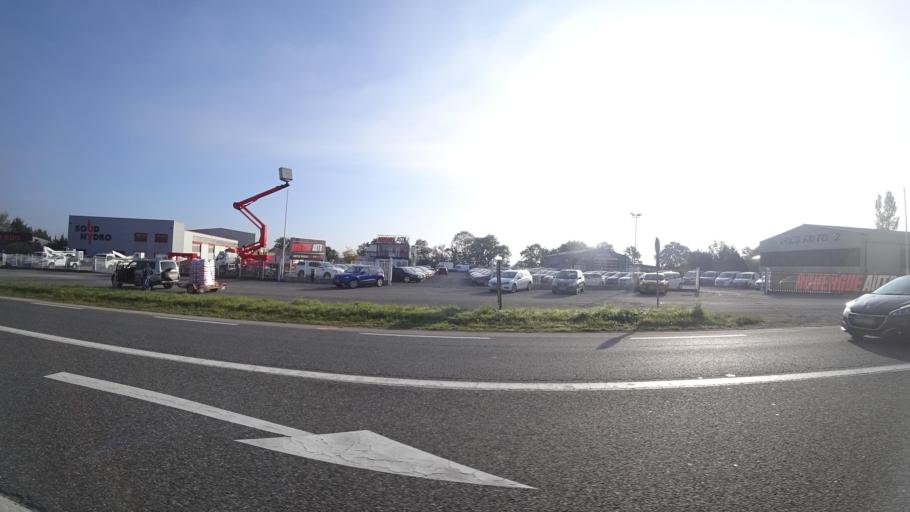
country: FR
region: Midi-Pyrenees
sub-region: Departement de l'Aveyron
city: Luc-la-Primaube
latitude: 44.3179
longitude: 2.5580
